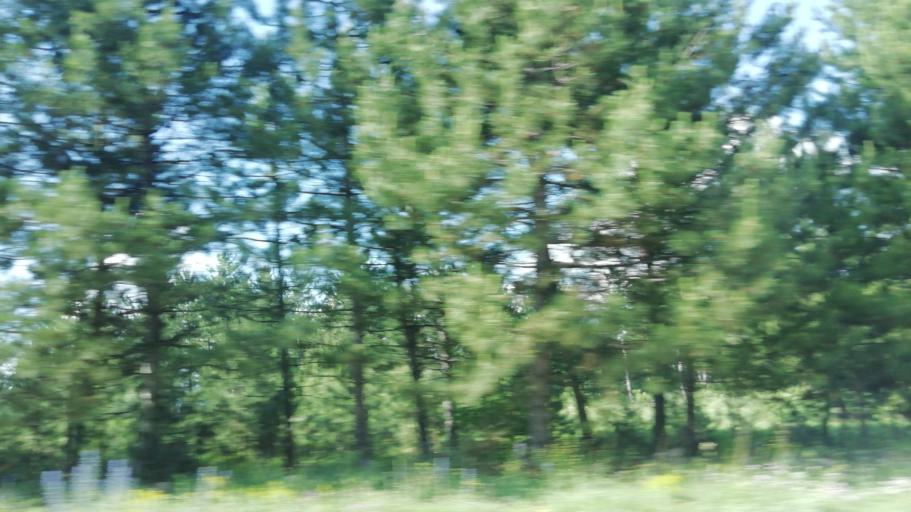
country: TR
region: Karabuk
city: Karabuk
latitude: 41.1258
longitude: 32.5944
